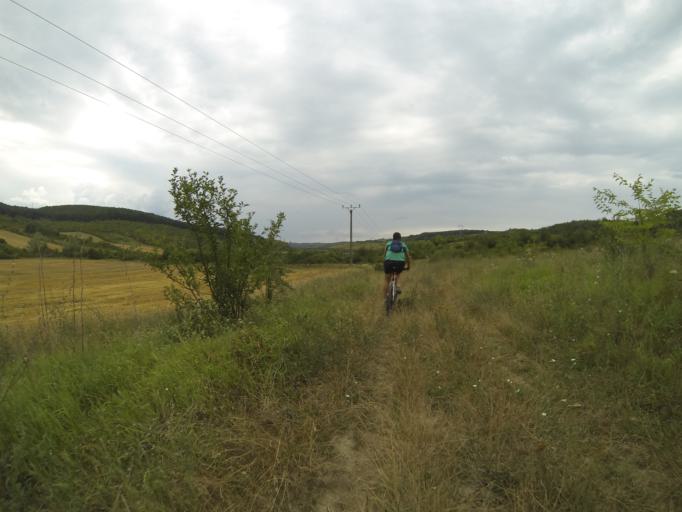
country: RO
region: Dolj
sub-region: Comuna Almaju
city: Almaju
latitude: 44.4762
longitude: 23.6922
